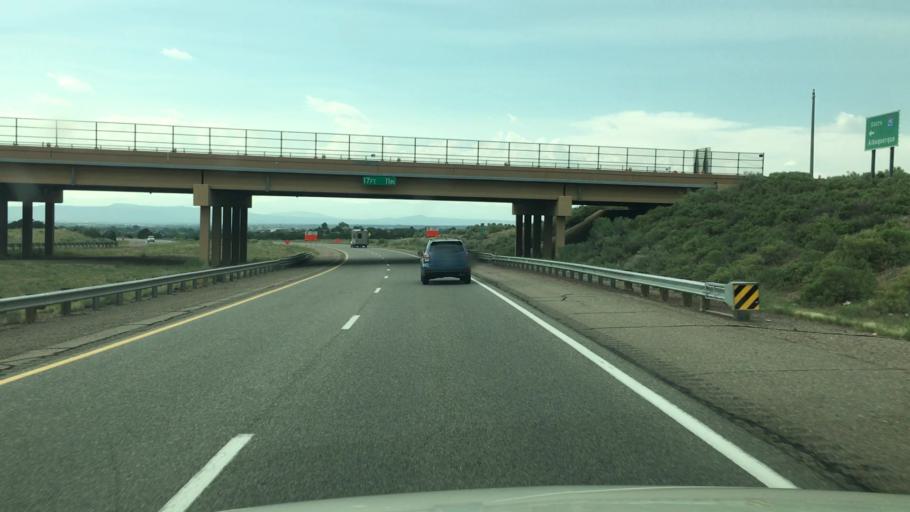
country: US
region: New Mexico
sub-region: Santa Fe County
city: Santa Fe
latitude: 35.6363
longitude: -105.9297
